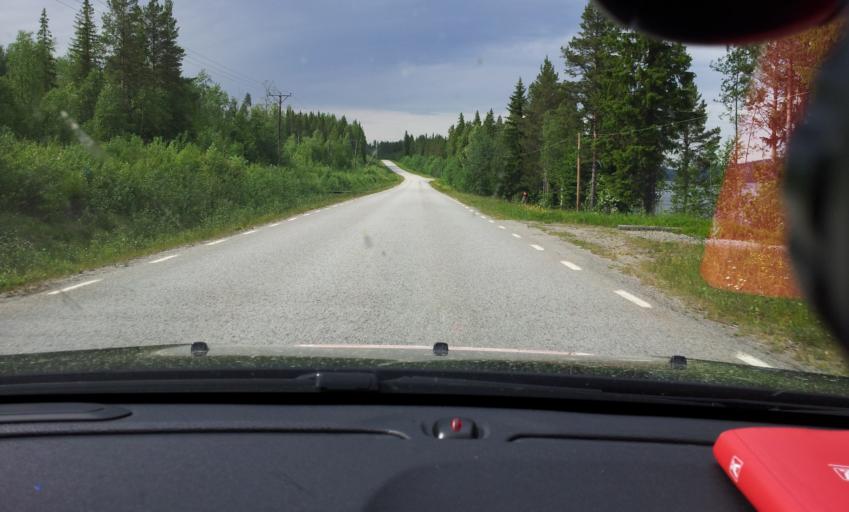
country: SE
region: Jaemtland
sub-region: Bergs Kommun
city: Hoverberg
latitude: 62.6617
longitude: 14.7360
